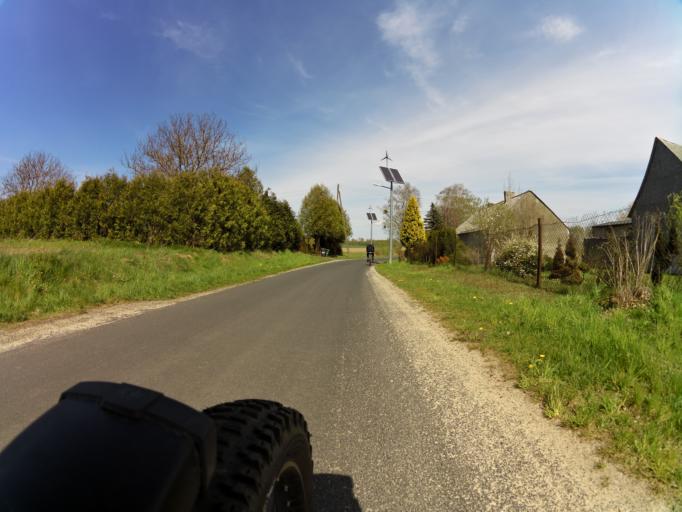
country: PL
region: West Pomeranian Voivodeship
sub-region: Powiat lobeski
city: Resko
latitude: 53.7899
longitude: 15.4276
